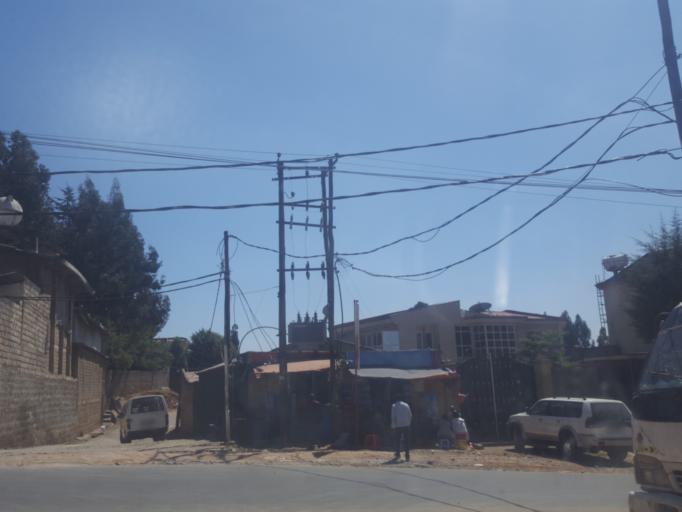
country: ET
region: Adis Abeba
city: Addis Ababa
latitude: 9.0568
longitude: 38.7251
